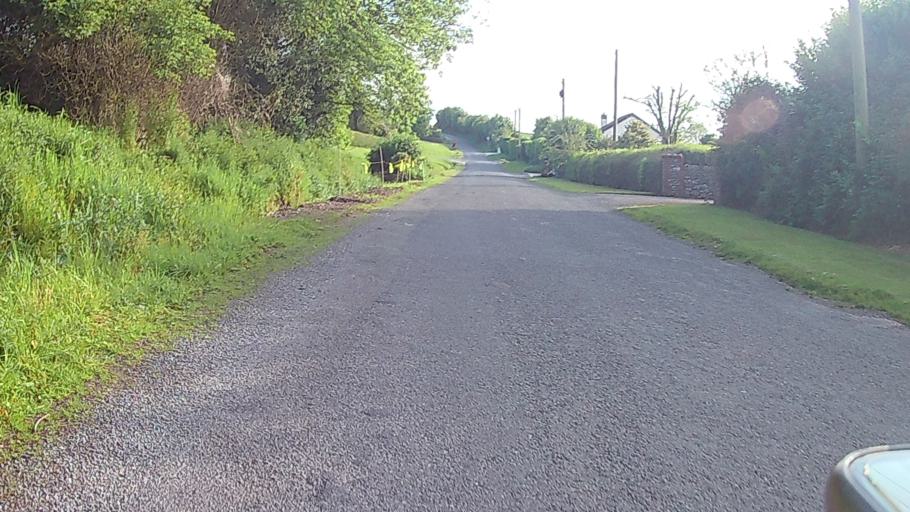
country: IE
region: Munster
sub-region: County Cork
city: Cork
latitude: 51.9728
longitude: -8.4625
